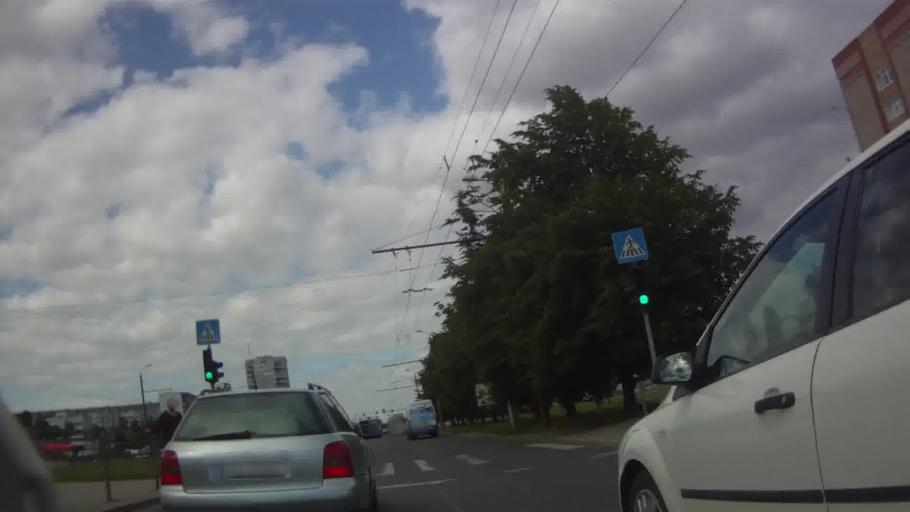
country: LV
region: Stopini
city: Ulbroka
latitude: 56.9376
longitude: 24.2034
